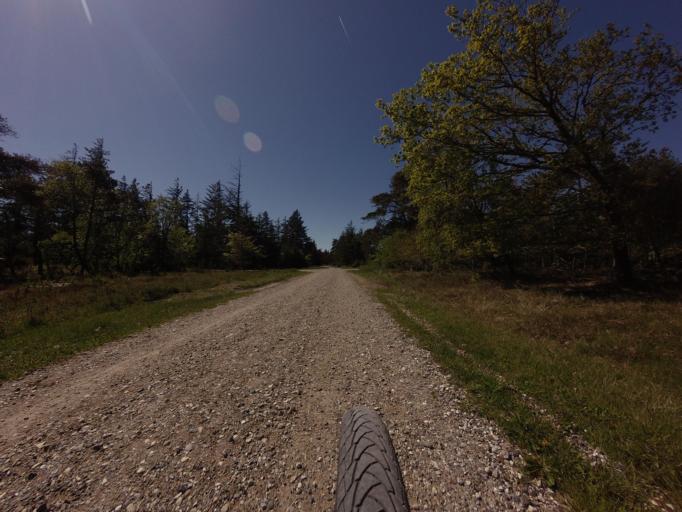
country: DK
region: North Denmark
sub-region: Jammerbugt Kommune
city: Pandrup
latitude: 57.2370
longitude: 9.5816
